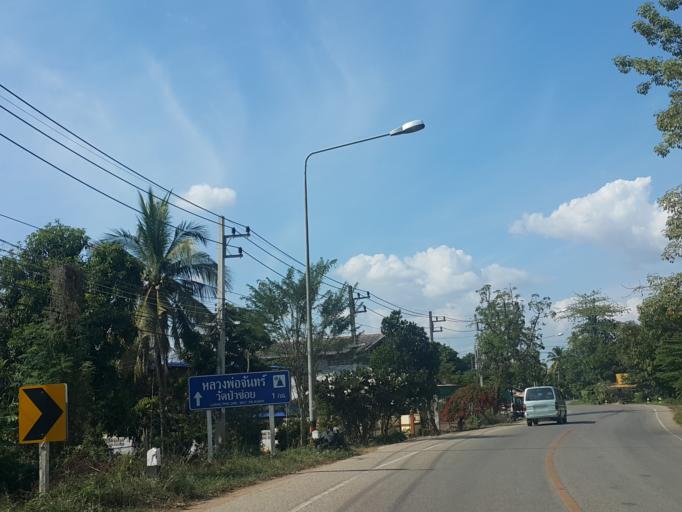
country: TH
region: Sukhothai
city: Sawankhalok
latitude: 17.2944
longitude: 99.8282
